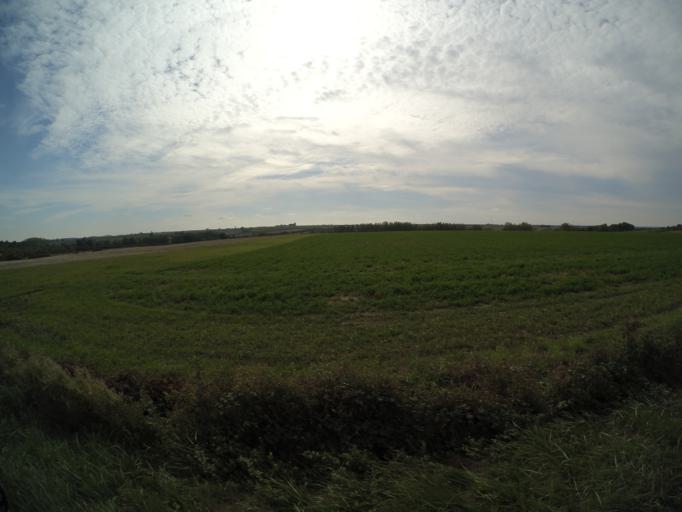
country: FR
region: Pays de la Loire
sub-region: Departement de Maine-et-Loire
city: Doue-la-Fontaine
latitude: 47.1923
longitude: -0.3336
